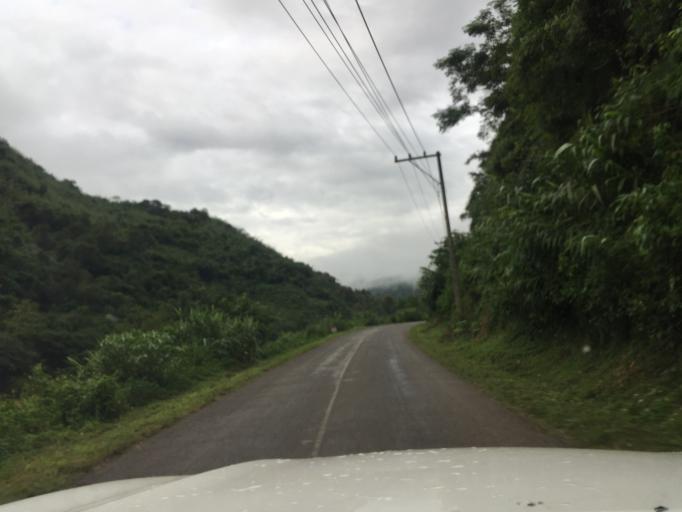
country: LA
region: Oudomxai
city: Muang La
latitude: 20.9146
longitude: 102.1939
